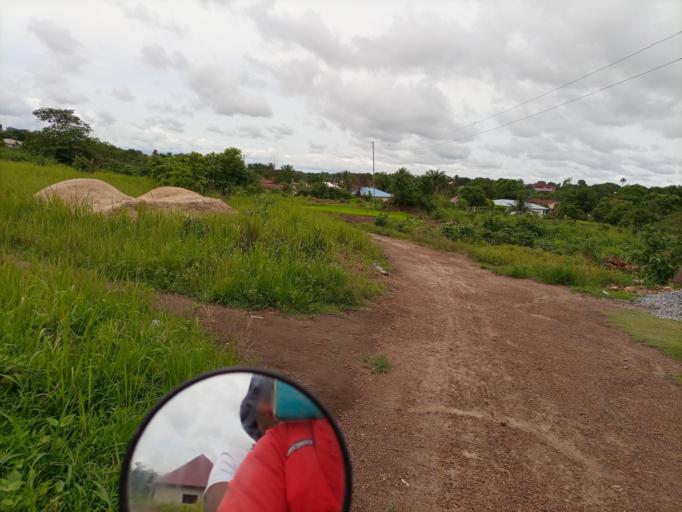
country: SL
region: Southern Province
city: Bo
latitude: 7.9426
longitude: -11.7470
